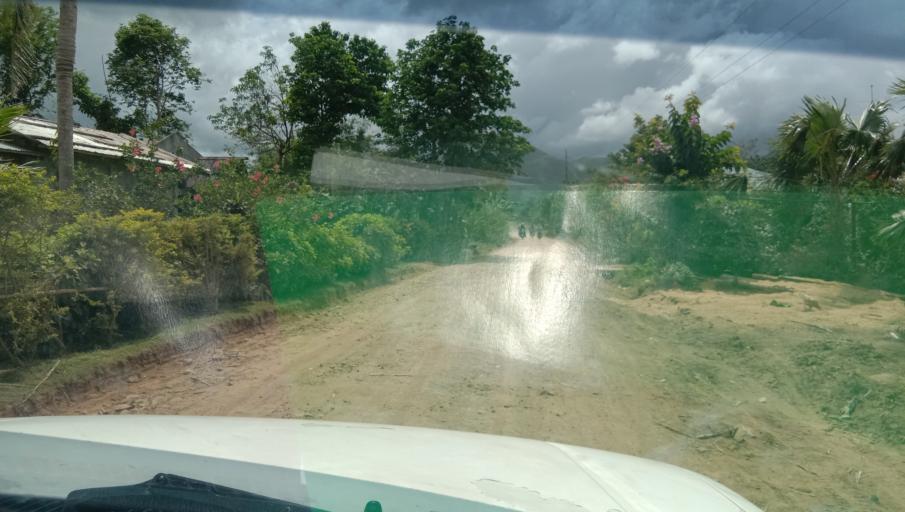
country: PH
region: Western Visayas
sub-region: Province of Iloilo
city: Balasan
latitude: 11.4698
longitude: 123.0584
